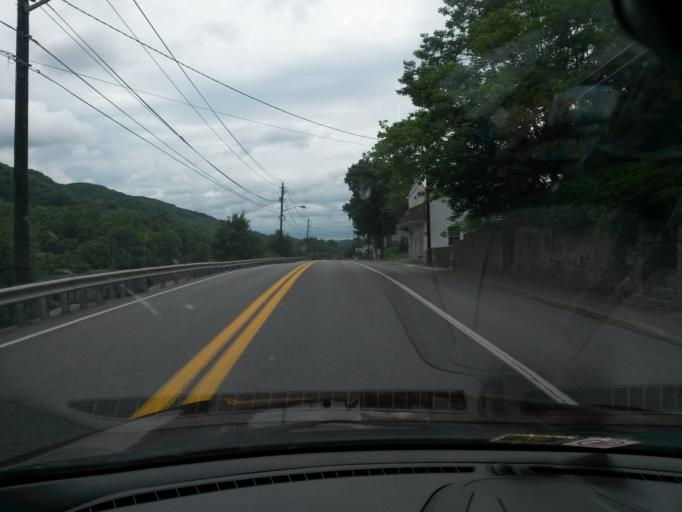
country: US
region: West Virginia
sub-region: Mercer County
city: Bluefield
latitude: 37.2768
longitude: -81.2009
